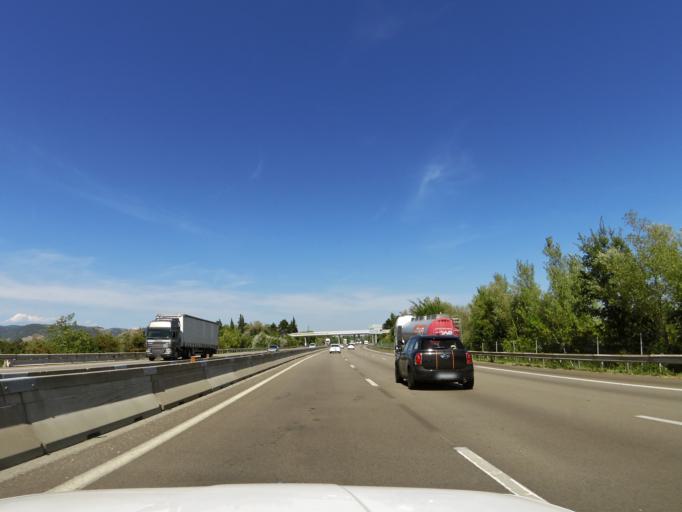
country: FR
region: Rhone-Alpes
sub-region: Departement de la Drome
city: Loriol-sur-Drome
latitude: 44.7474
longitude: 4.7895
